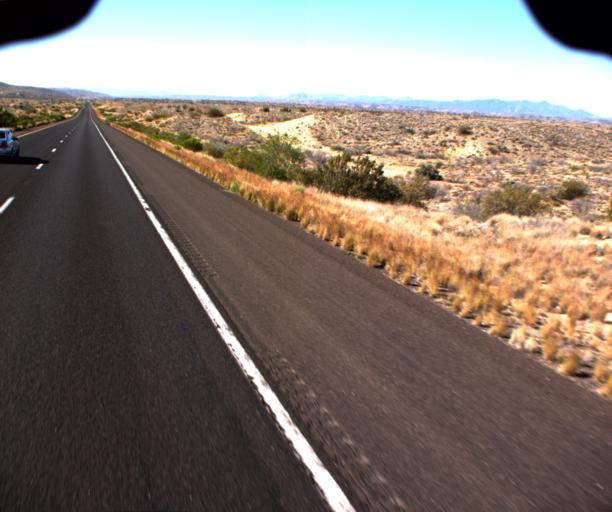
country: US
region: Arizona
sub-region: Mohave County
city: Kingman
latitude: 35.0662
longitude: -113.6658
